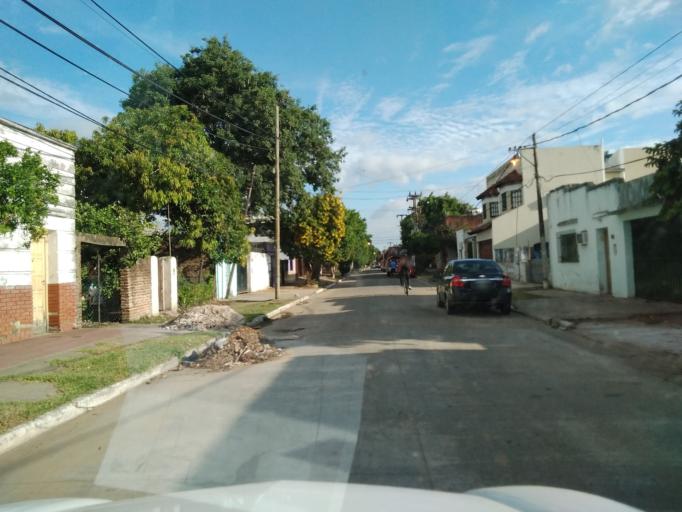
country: AR
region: Corrientes
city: Corrientes
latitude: -27.4625
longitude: -58.8193
